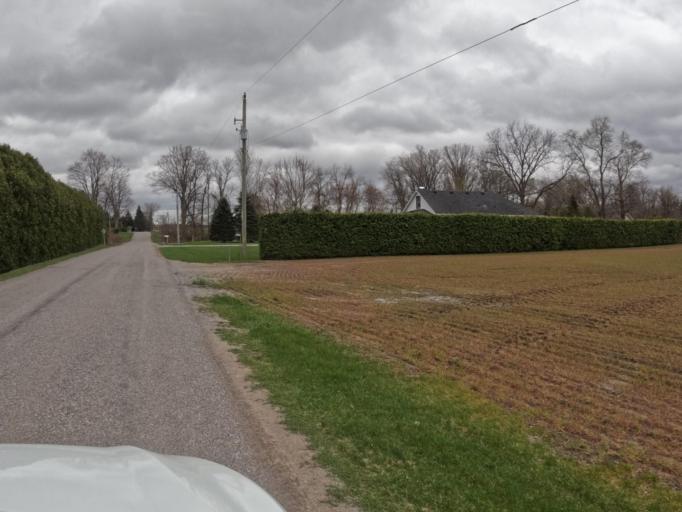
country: CA
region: Ontario
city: Norfolk County
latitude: 42.9675
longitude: -80.4296
